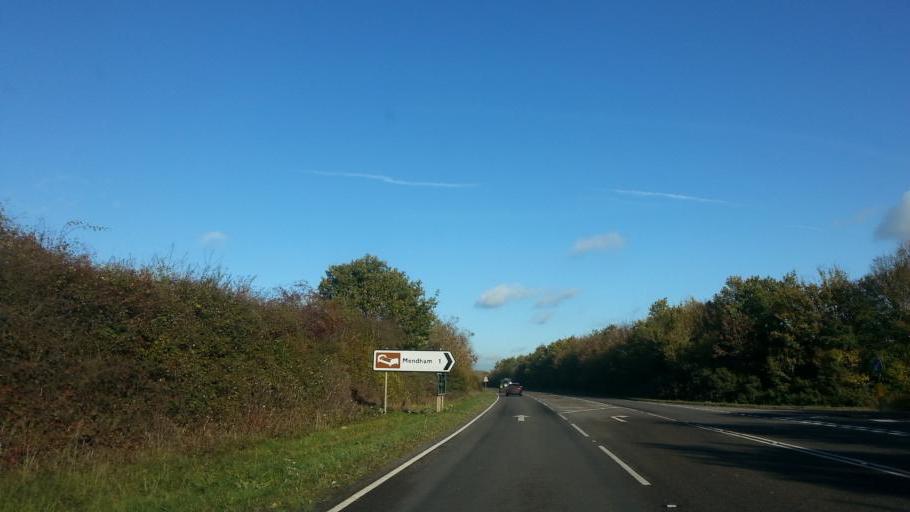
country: GB
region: England
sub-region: Norfolk
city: Harleston
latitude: 52.3970
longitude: 1.3100
